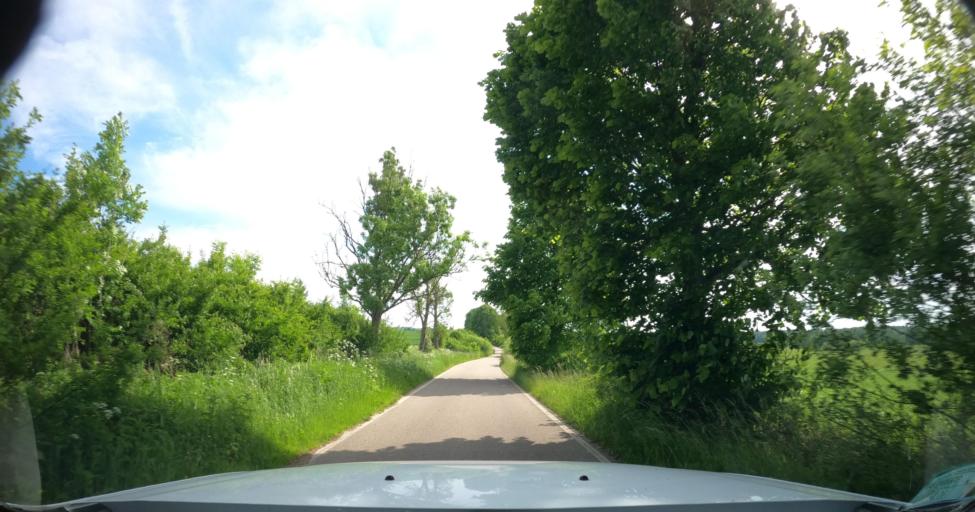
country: PL
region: Warmian-Masurian Voivodeship
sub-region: Powiat ostrodzki
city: Milakowo
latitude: 54.0195
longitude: 20.1593
